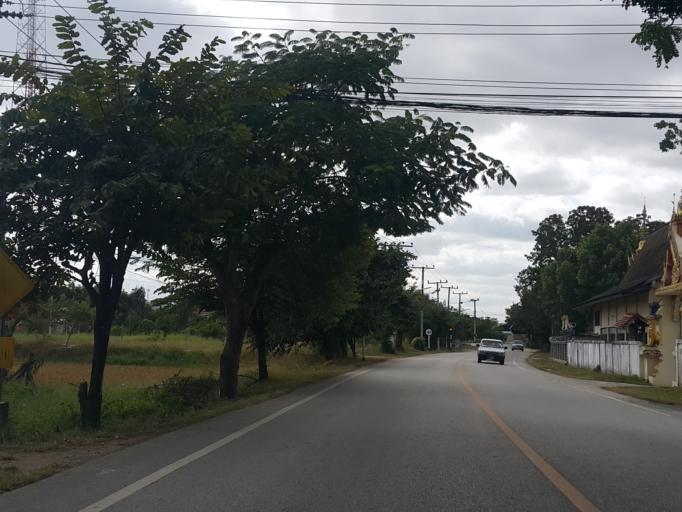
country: TH
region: Lamphun
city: Ban Thi
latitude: 18.6493
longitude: 99.1094
